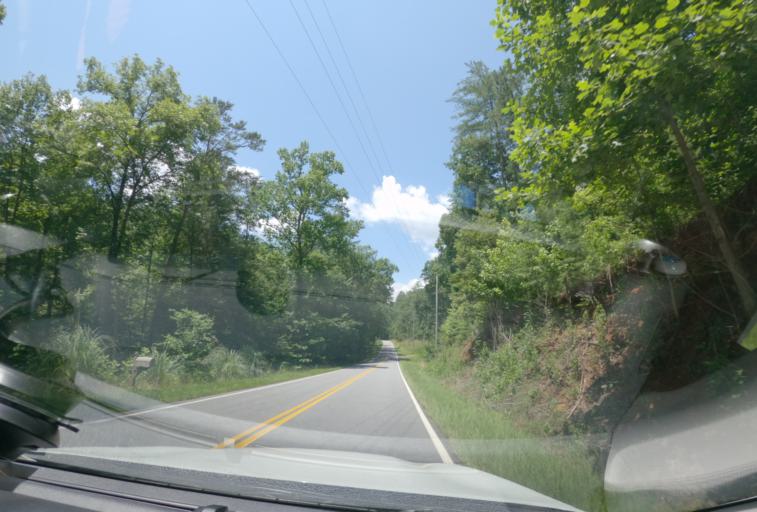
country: US
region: South Carolina
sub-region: Pickens County
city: Pickens
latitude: 34.9583
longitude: -82.8485
